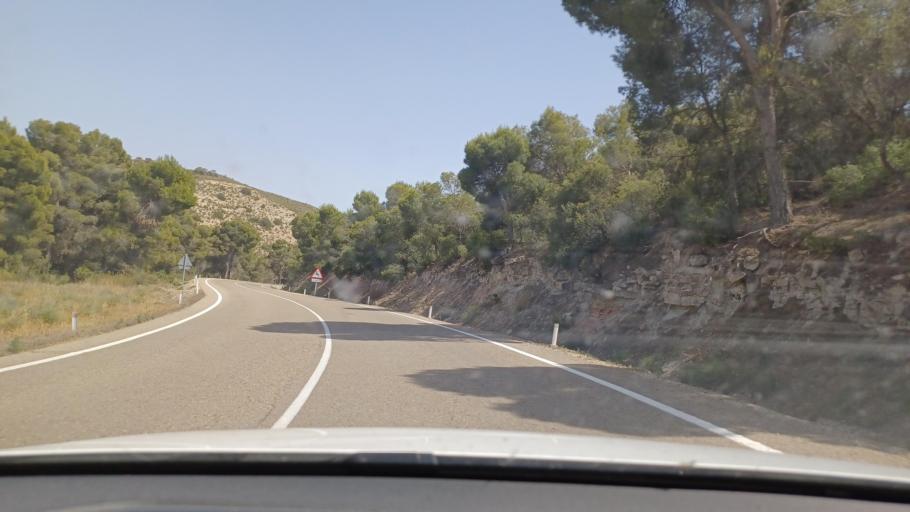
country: ES
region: Aragon
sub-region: Provincia de Zaragoza
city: Chiprana
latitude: 41.3582
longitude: -0.1022
